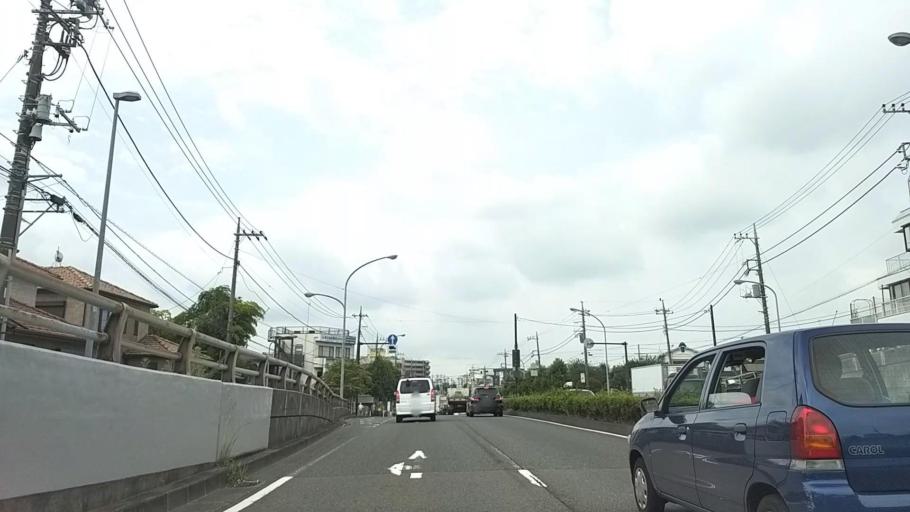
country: JP
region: Kanagawa
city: Minami-rinkan
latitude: 35.4698
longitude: 139.4956
